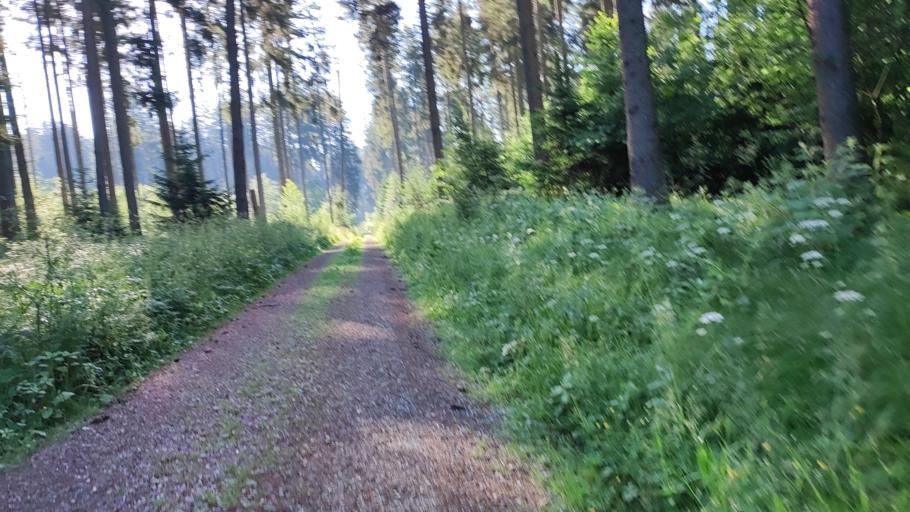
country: DE
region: Bavaria
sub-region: Swabia
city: Horgau
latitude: 48.3799
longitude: 10.7077
